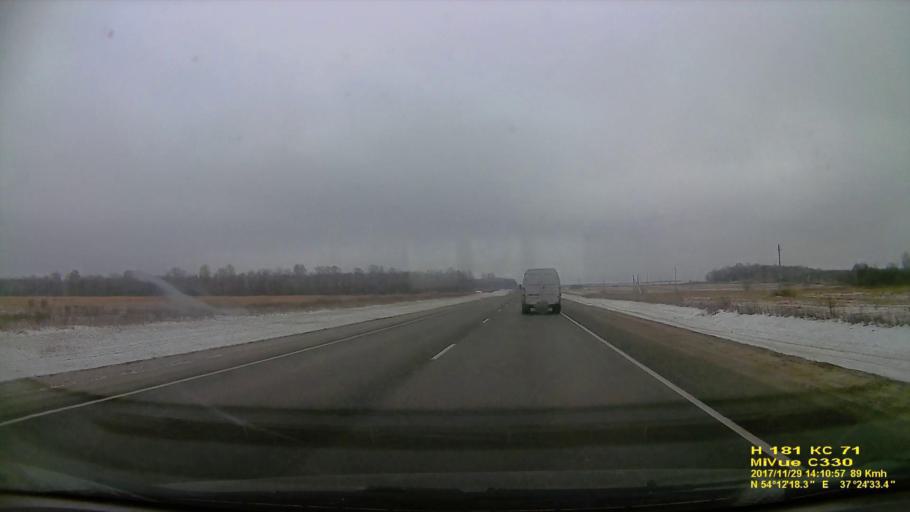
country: RU
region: Tula
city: Leninskiy
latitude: 54.2048
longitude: 37.4097
